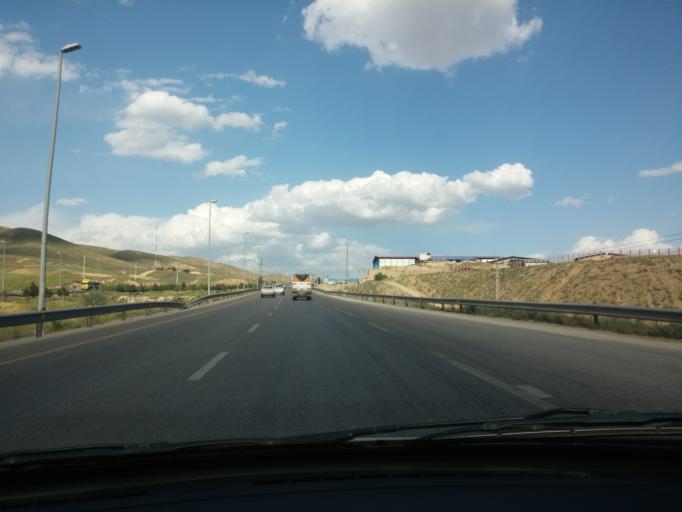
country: IR
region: Tehran
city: Damavand
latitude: 35.7076
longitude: 51.9722
